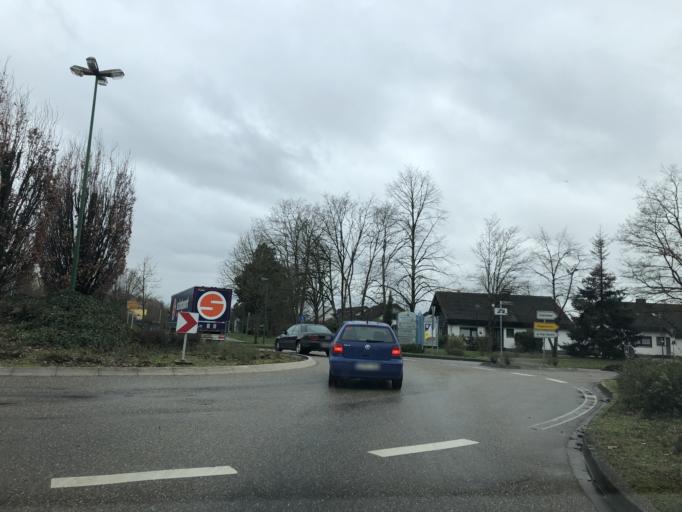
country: DE
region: Baden-Wuerttemberg
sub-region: Karlsruhe Region
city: Muggensturm
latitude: 48.8762
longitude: 8.2916
